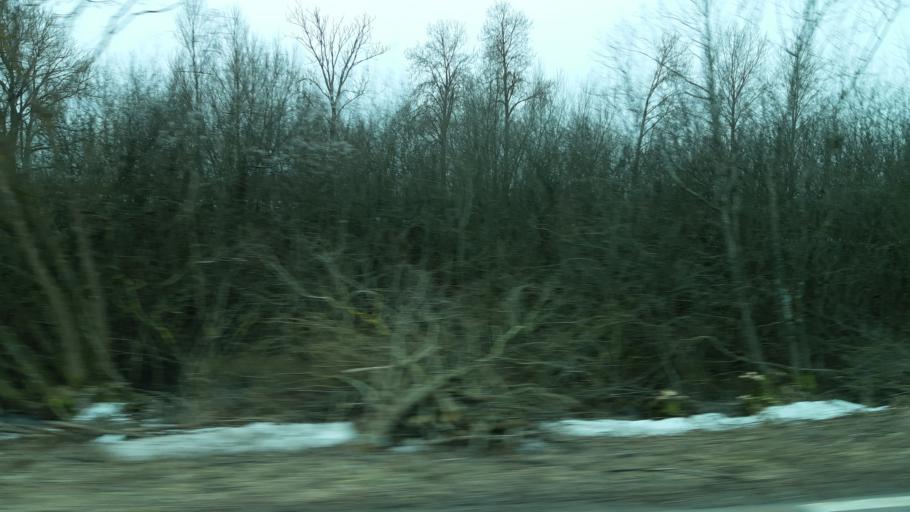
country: PL
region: Podlasie
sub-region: Suwalki
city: Suwalki
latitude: 54.3315
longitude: 22.9467
